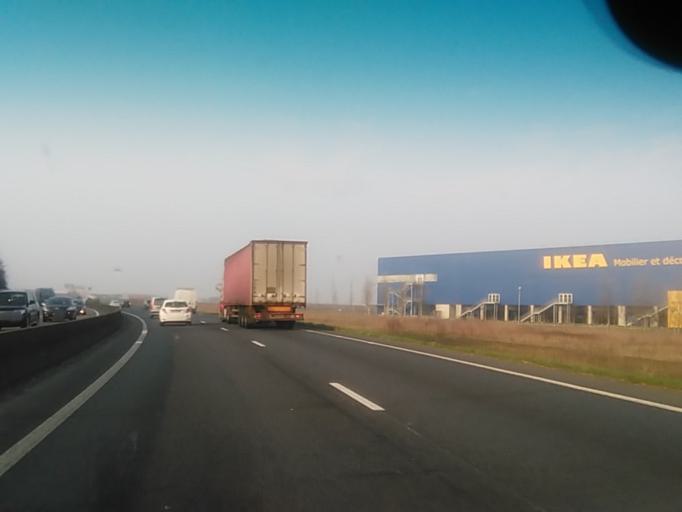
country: FR
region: Lower Normandy
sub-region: Departement du Calvados
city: Ifs
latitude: 49.1461
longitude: -0.3600
